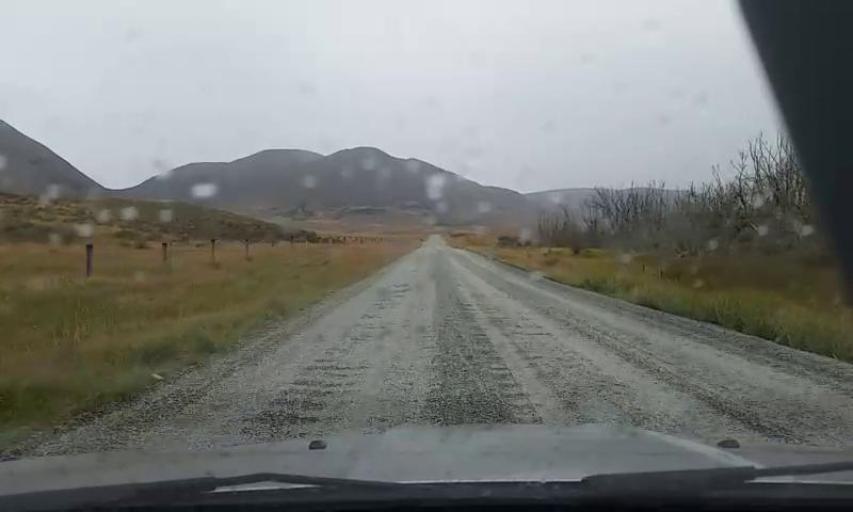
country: NZ
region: Canterbury
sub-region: Ashburton District
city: Methven
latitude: -43.6158
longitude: 171.0913
